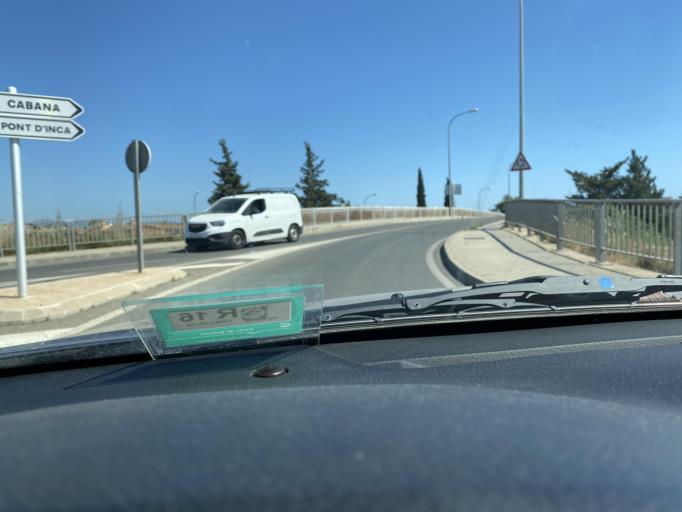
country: ES
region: Balearic Islands
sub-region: Illes Balears
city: Palma
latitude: 39.6069
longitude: 2.6857
